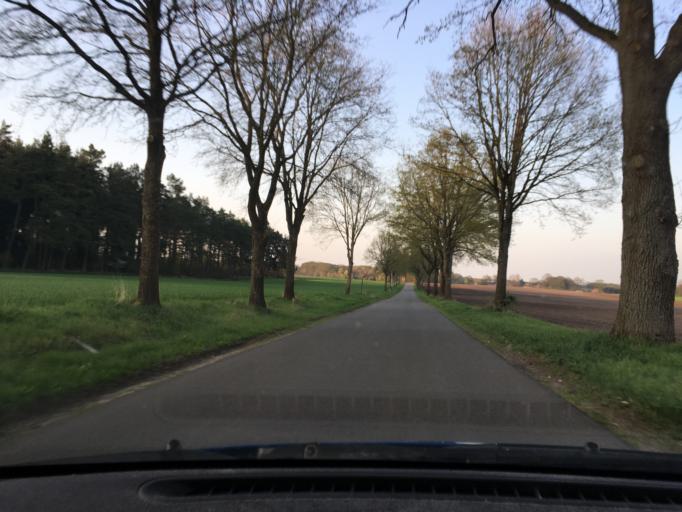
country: DE
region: Lower Saxony
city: Sudergellersen
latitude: 53.1972
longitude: 10.2824
